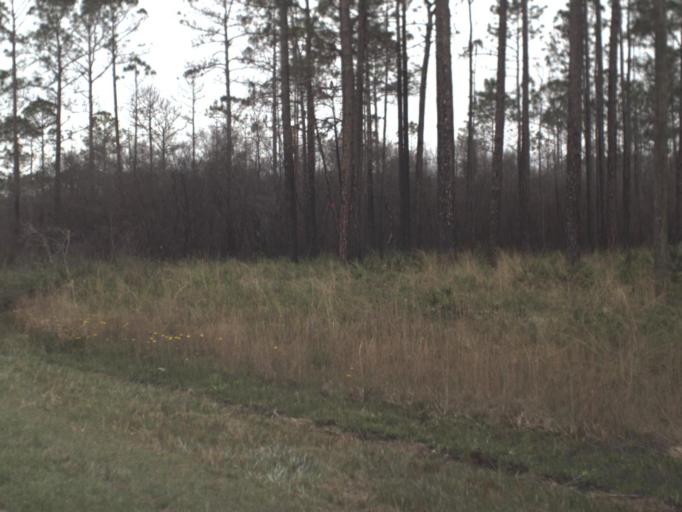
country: US
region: Florida
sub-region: Gulf County
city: Wewahitchka
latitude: 30.1439
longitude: -84.9765
